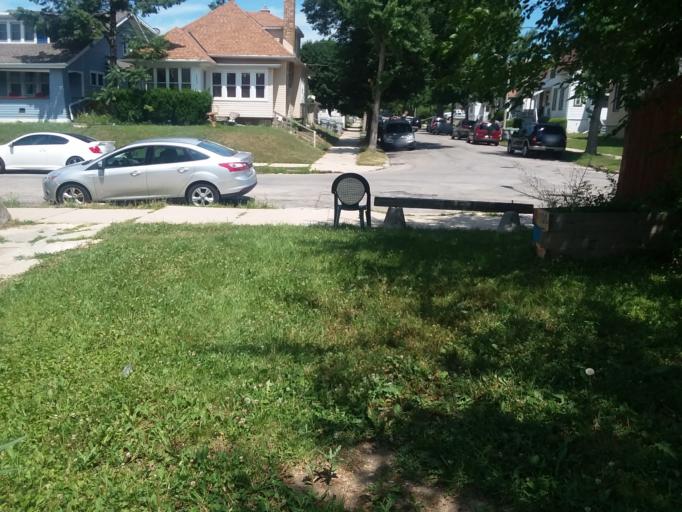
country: US
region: Wisconsin
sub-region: Milwaukee County
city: West Milwaukee
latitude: 43.0176
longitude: -87.9540
